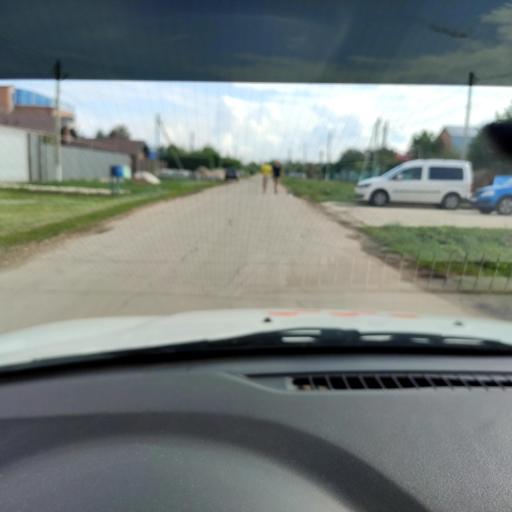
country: RU
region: Samara
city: Podstepki
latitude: 53.6074
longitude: 49.0387
